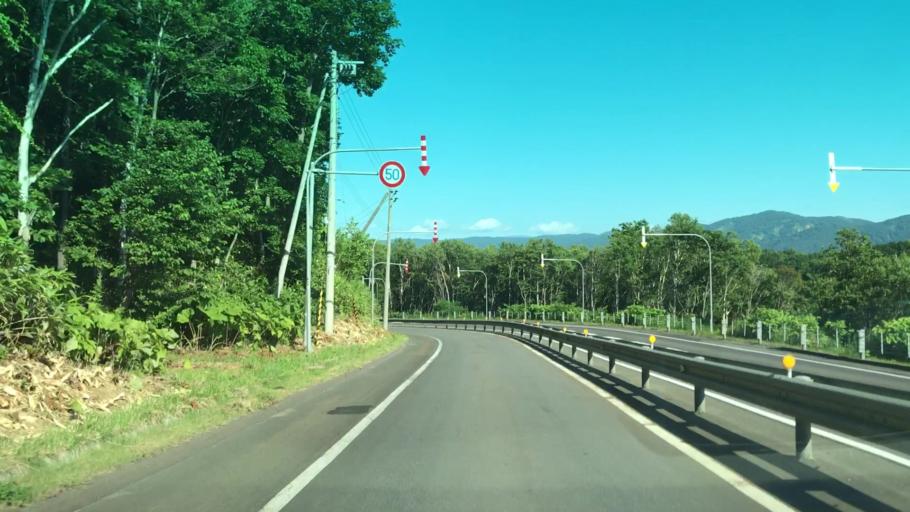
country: JP
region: Hokkaido
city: Yoichi
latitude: 43.0642
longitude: 140.6967
